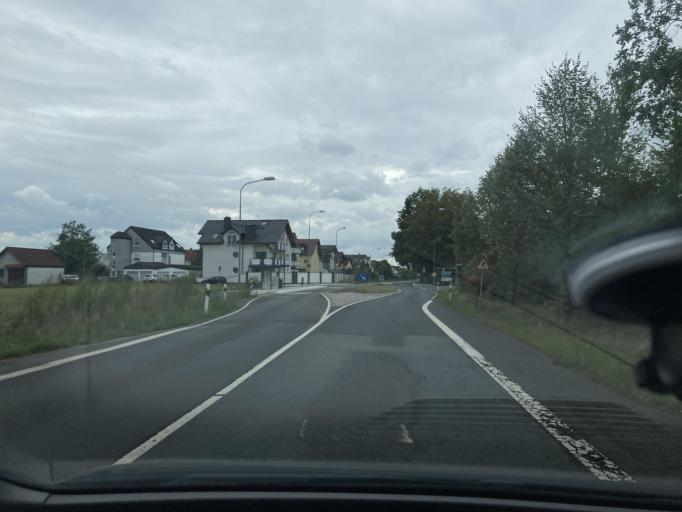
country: DE
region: Bavaria
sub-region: Regierungsbezirk Unterfranken
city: Kahl am Main
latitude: 50.0387
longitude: 9.0168
